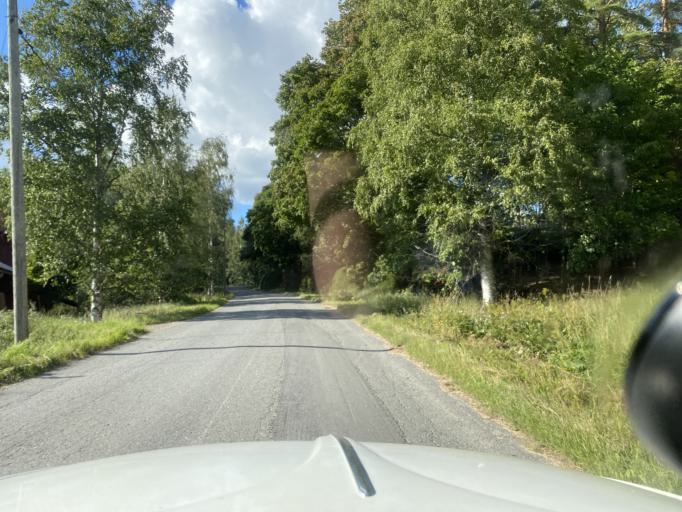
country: FI
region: Pirkanmaa
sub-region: Lounais-Pirkanmaa
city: Punkalaidun
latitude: 61.1459
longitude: 23.1971
